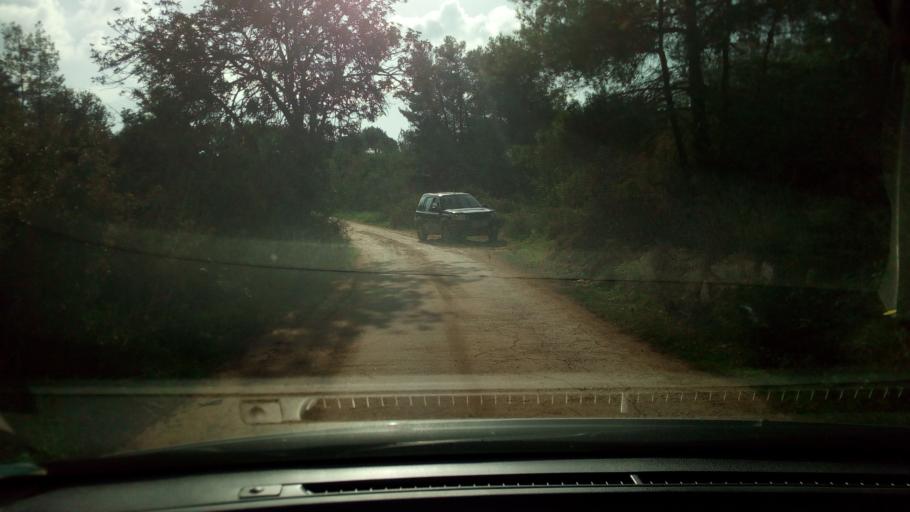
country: CY
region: Pafos
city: Polis
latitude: 35.0219
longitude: 32.3551
